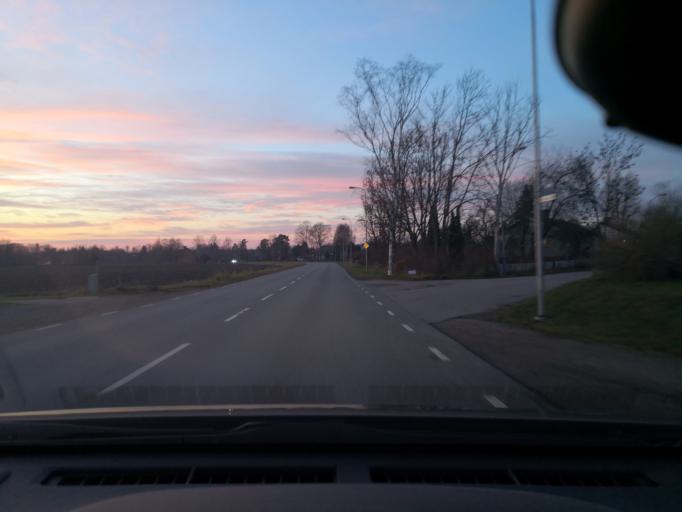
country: SE
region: OErebro
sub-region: Lindesbergs Kommun
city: Fellingsbro
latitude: 59.4294
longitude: 15.5926
